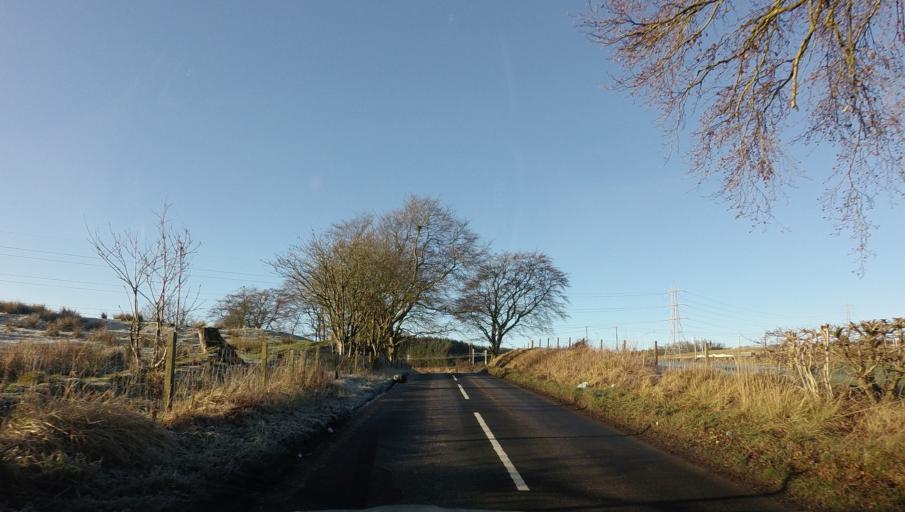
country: GB
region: Scotland
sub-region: North Lanarkshire
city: Shotts
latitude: 55.8052
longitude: -3.8468
